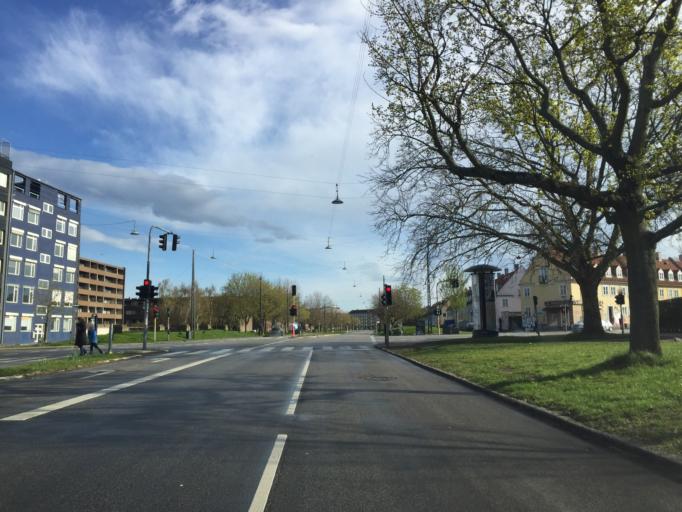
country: DK
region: Capital Region
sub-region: Kobenhavn
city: Copenhagen
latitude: 55.7082
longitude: 12.5561
